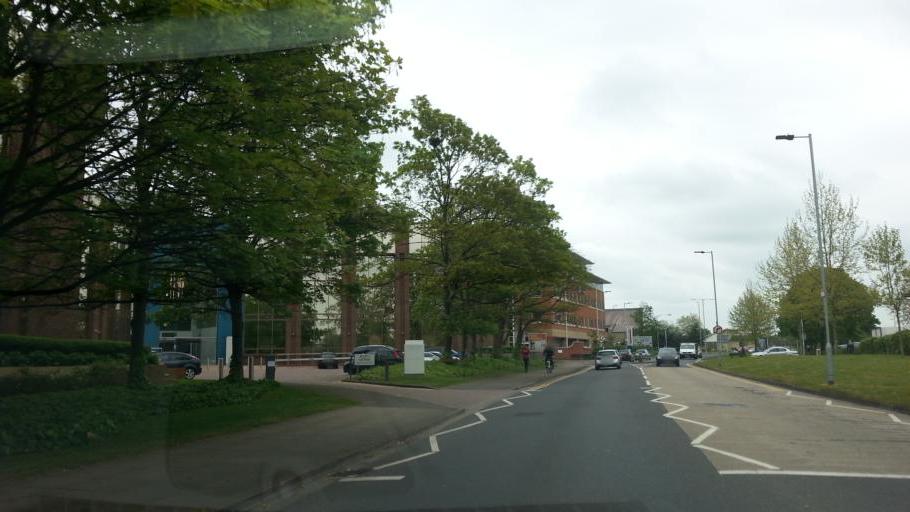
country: GB
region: England
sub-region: Peterborough
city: Peterborough
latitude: 52.5748
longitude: -0.2360
